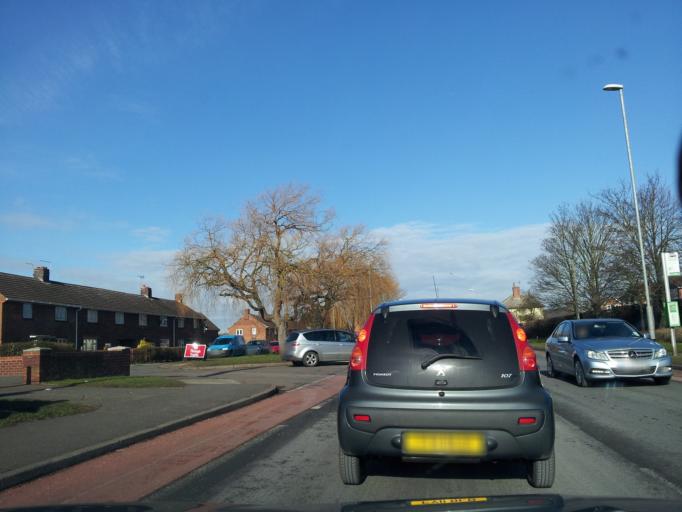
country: GB
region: England
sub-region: Nottinghamshire
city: Newark on Trent
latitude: 53.0540
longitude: -0.7837
